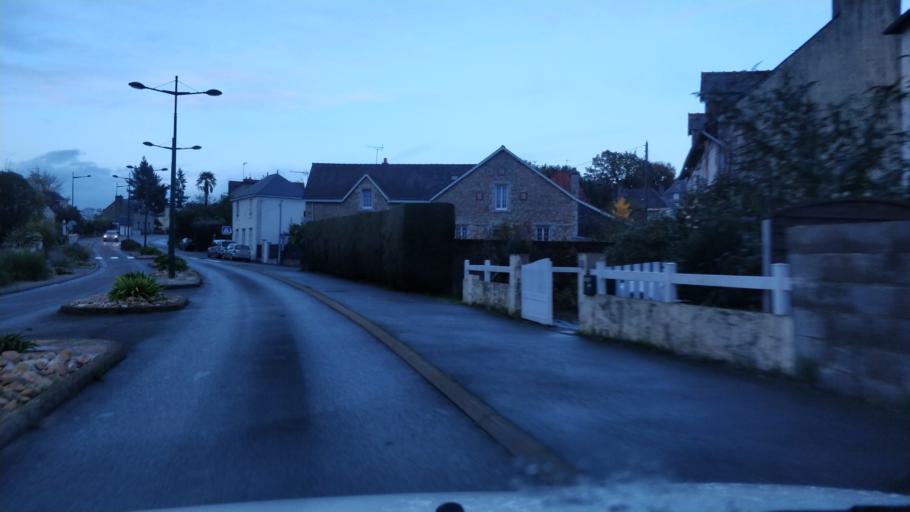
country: FR
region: Brittany
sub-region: Departement du Morbihan
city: Pontivy
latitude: 48.0757
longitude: -2.9573
